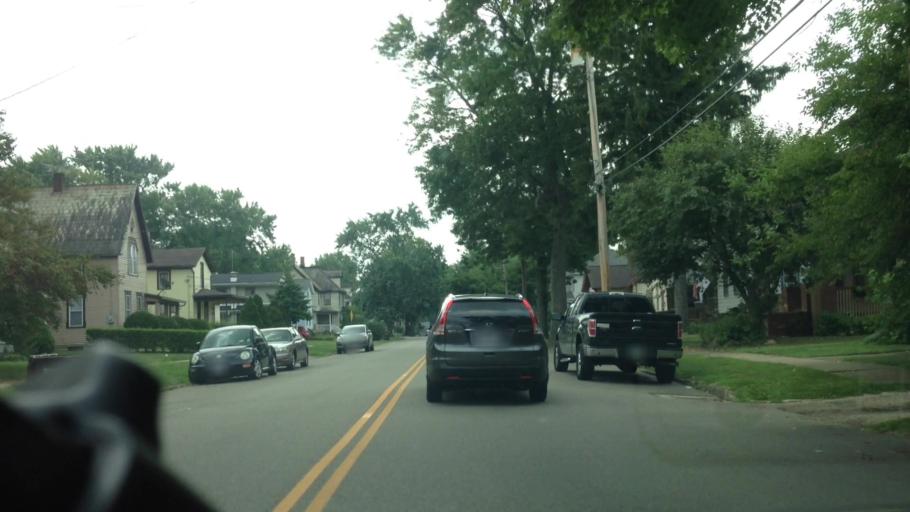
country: US
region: Ohio
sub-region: Stark County
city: Massillon
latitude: 40.8031
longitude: -81.5158
